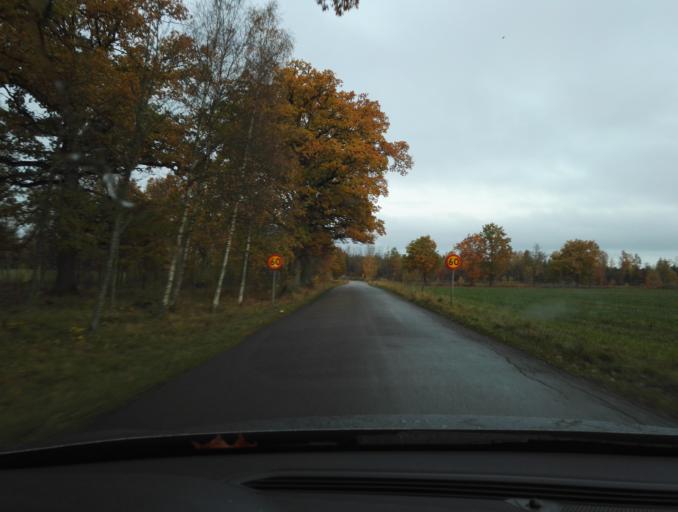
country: SE
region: Kronoberg
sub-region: Vaxjo Kommun
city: Vaexjoe
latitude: 56.9144
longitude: 14.7348
